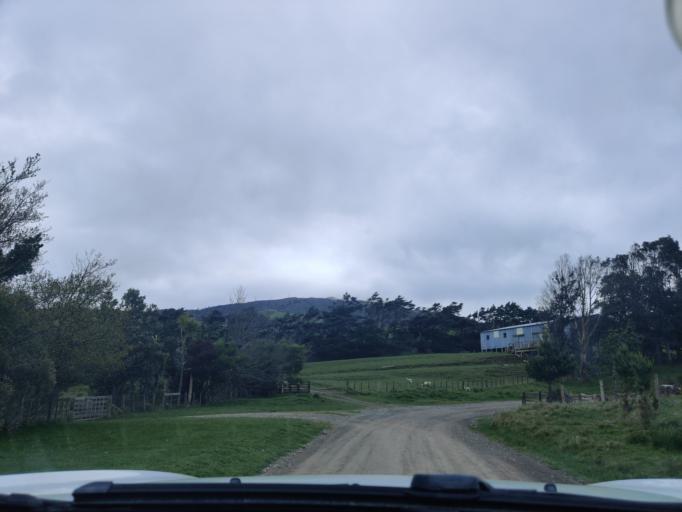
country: NZ
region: Manawatu-Wanganui
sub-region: Palmerston North City
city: Palmerston North
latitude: -40.2868
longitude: 175.8604
